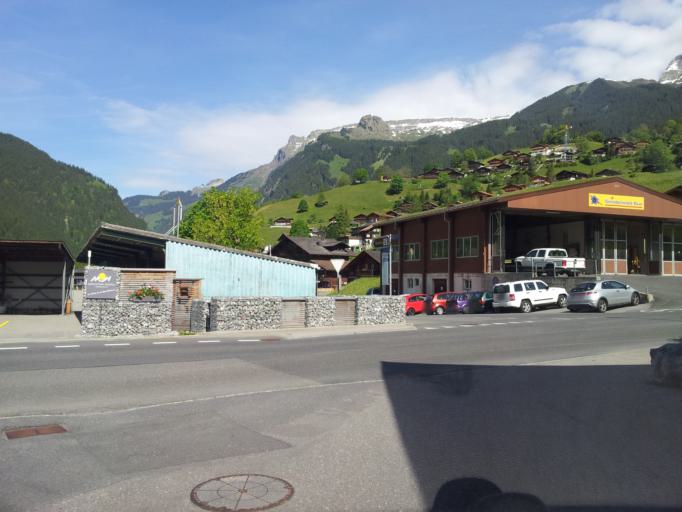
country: CH
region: Bern
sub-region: Interlaken-Oberhasli District
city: Grindelwald
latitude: 46.6236
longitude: 8.0227
